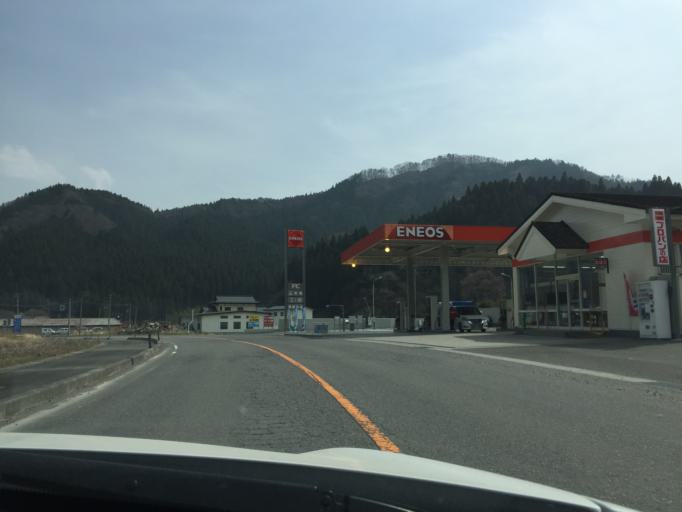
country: JP
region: Fukushima
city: Ishikawa
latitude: 37.0579
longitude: 140.5844
